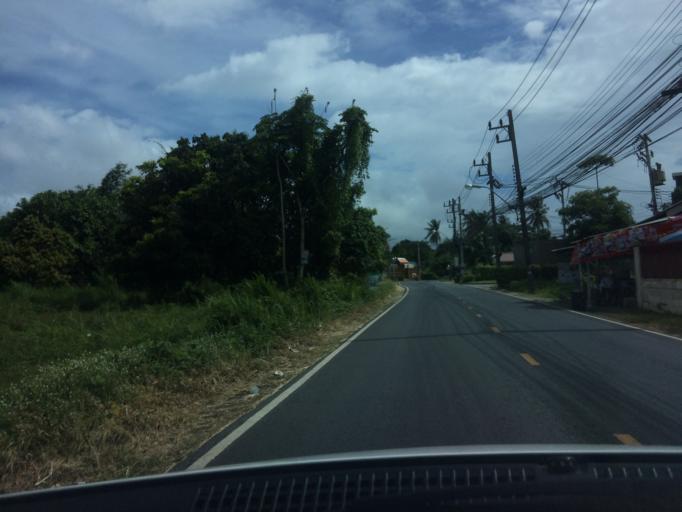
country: TH
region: Phuket
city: Thalang
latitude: 8.0305
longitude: 98.3410
